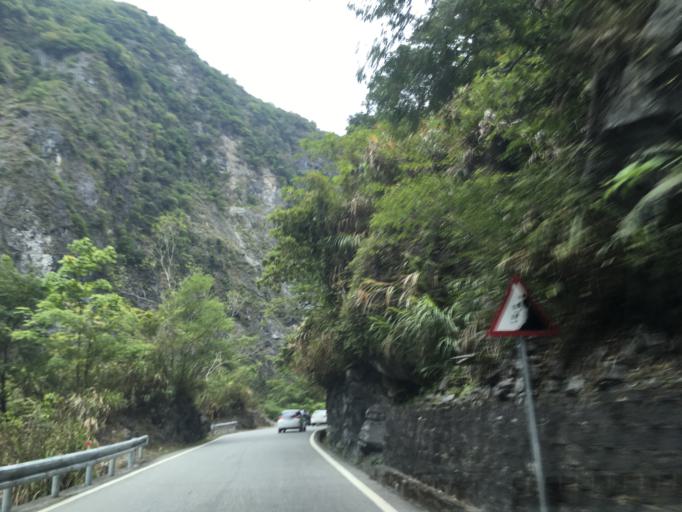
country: TW
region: Taiwan
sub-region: Hualien
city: Hualian
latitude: 24.1737
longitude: 121.5253
